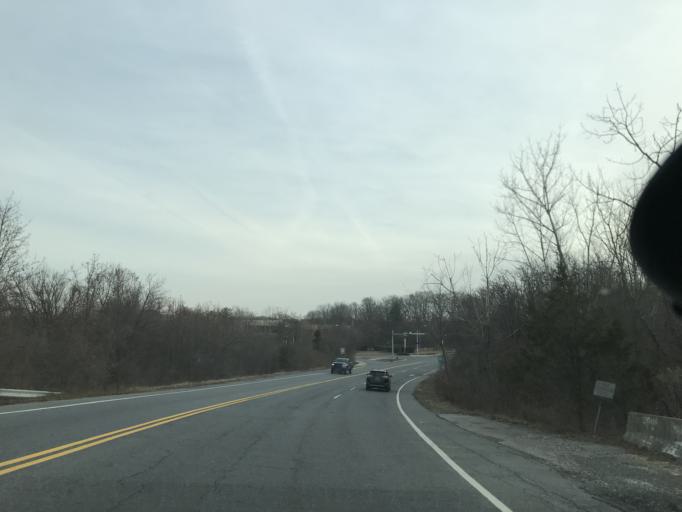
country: US
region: Maryland
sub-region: Prince George's County
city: Glenarden
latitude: 38.9458
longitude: -76.8695
